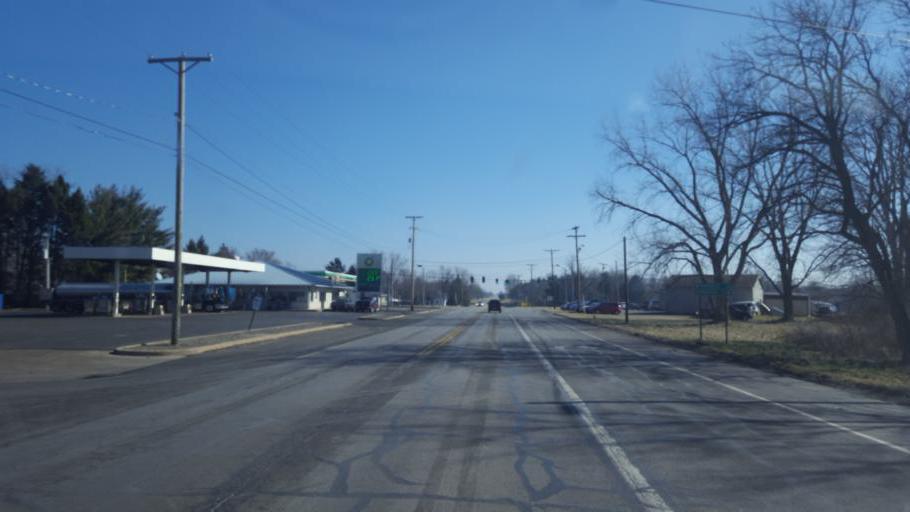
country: US
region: Ohio
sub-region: Huron County
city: Plymouth
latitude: 41.0317
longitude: -82.6832
